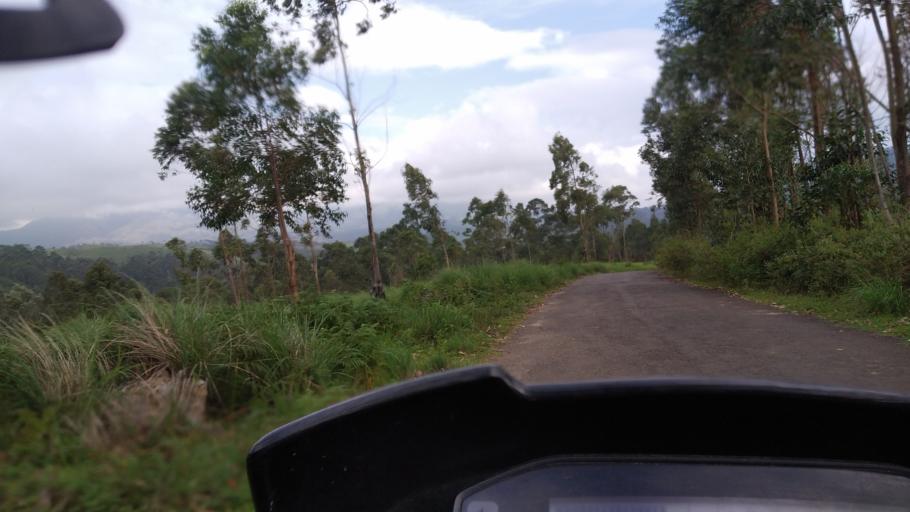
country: IN
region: Kerala
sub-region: Idukki
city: Munnar
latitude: 10.0350
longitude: 77.1896
